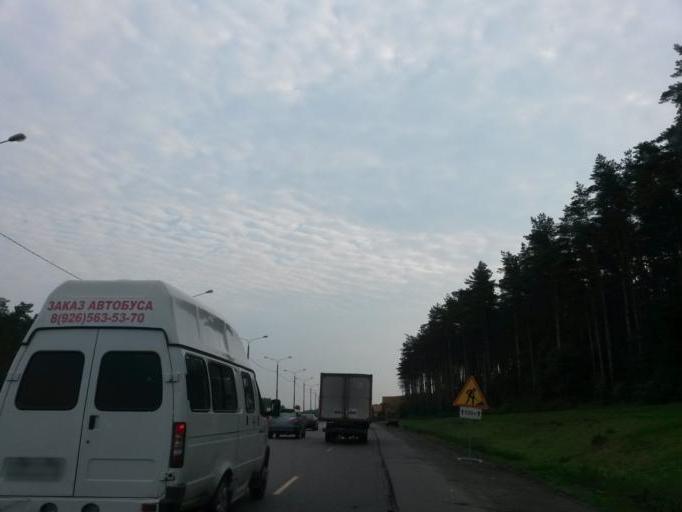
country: RU
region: Moskovskaya
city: Klimovsk
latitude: 55.3601
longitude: 37.5993
